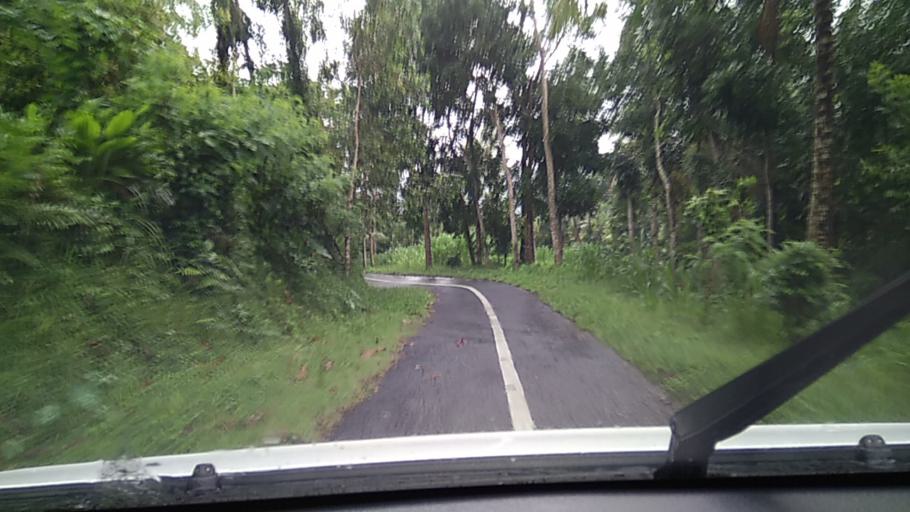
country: ID
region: Bali
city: Tiyingtali Kelod
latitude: -8.4006
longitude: 115.6297
